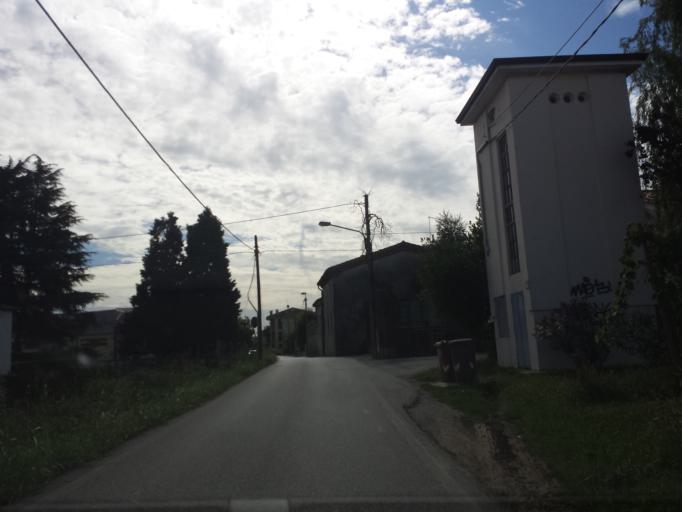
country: IT
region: Veneto
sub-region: Provincia di Vicenza
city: Vicenza
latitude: 45.5616
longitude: 11.5719
